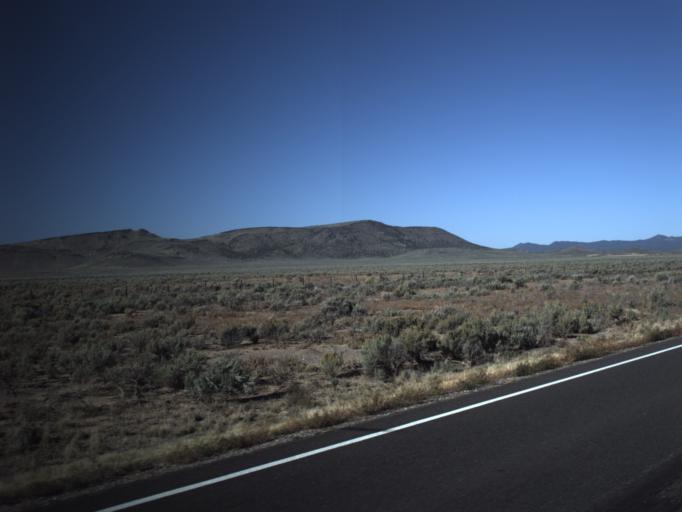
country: US
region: Utah
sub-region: Washington County
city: Enterprise
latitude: 37.7771
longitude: -113.8486
